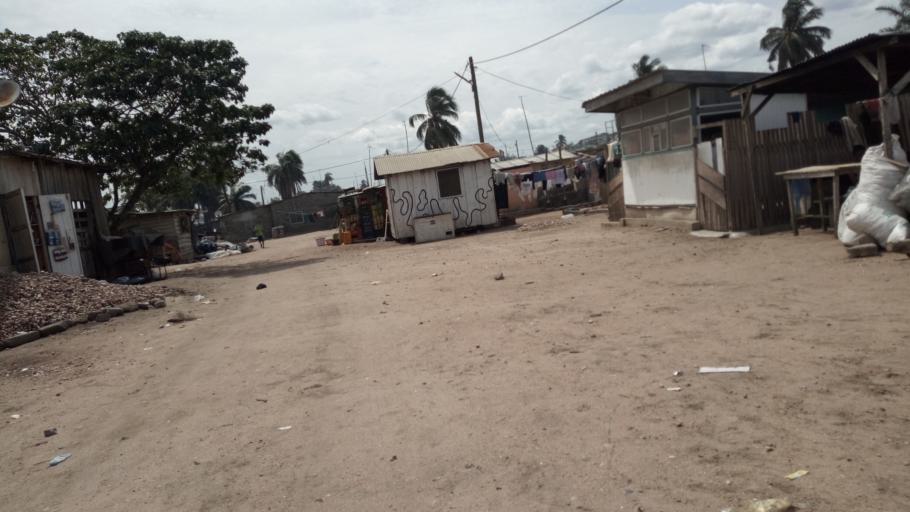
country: GH
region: Central
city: Winneba
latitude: 5.3486
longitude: -0.6167
